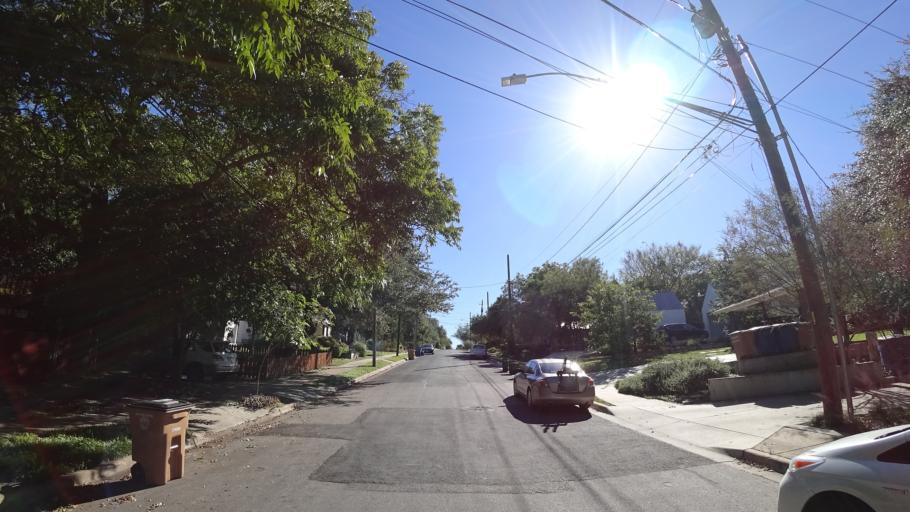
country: US
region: Texas
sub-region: Travis County
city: Austin
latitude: 30.2455
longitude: -97.7559
